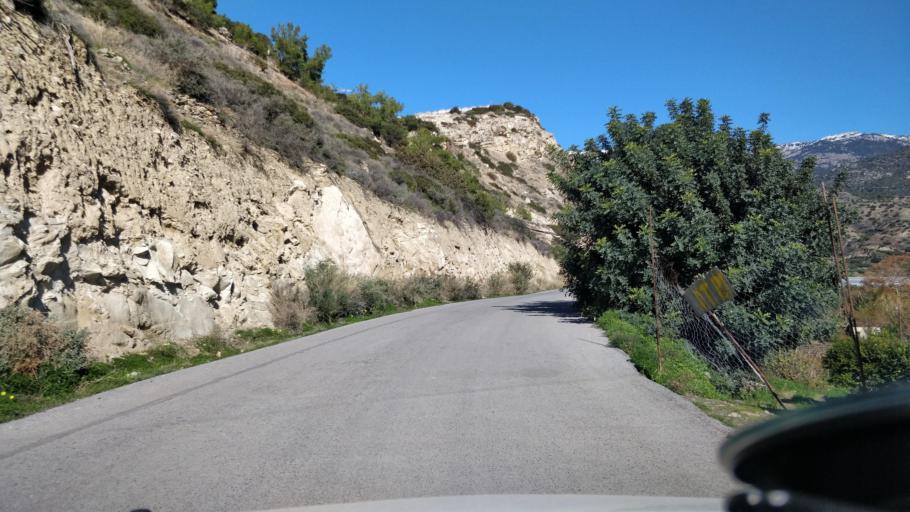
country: GR
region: Crete
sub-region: Nomos Lasithiou
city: Gra Liyia
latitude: 34.9881
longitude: 25.4812
